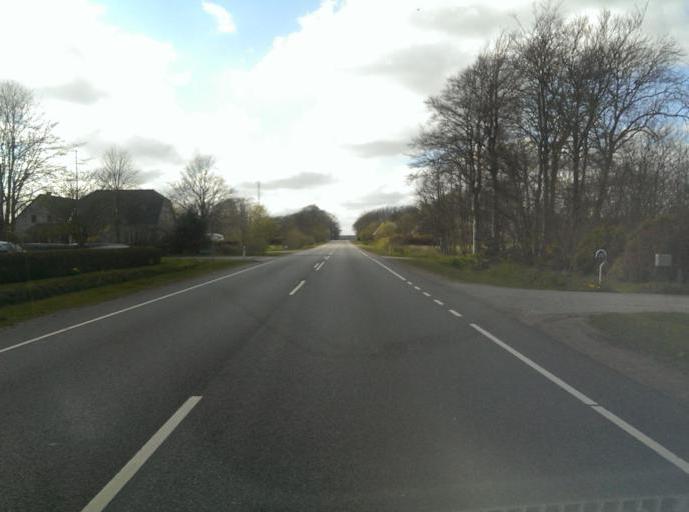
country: DK
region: South Denmark
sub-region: Esbjerg Kommune
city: Tjaereborg
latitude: 55.4905
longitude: 8.6330
